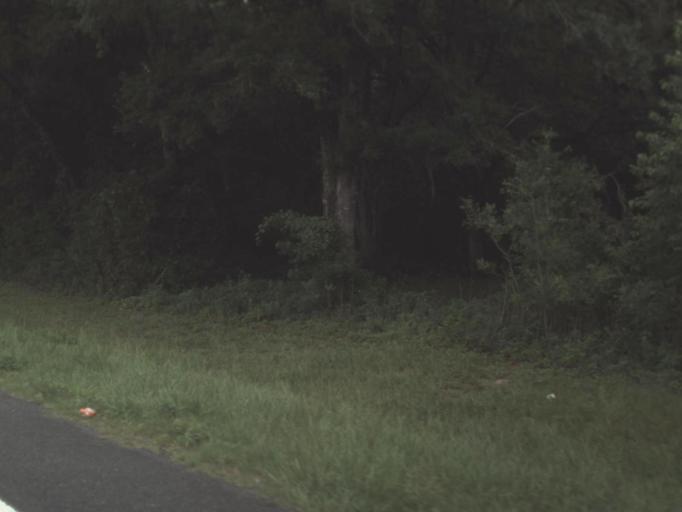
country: US
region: Florida
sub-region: Levy County
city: Williston Highlands
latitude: 29.2448
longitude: -82.4413
